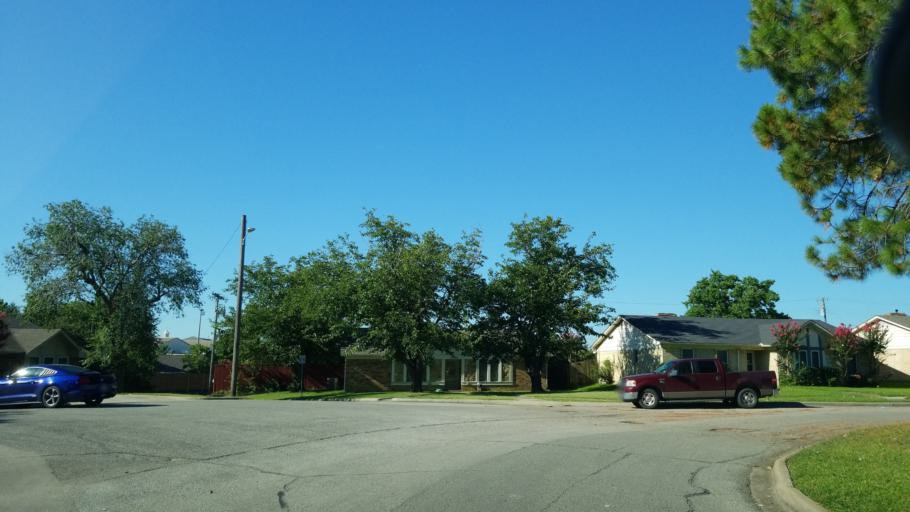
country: US
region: Texas
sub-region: Dallas County
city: Carrollton
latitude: 32.9425
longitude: -96.8855
